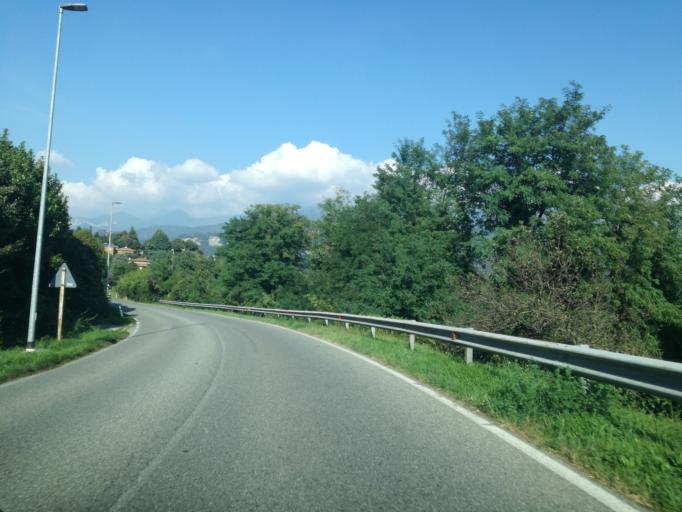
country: IT
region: Lombardy
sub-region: Provincia di Lecco
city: Brivio
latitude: 45.7331
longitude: 9.4436
